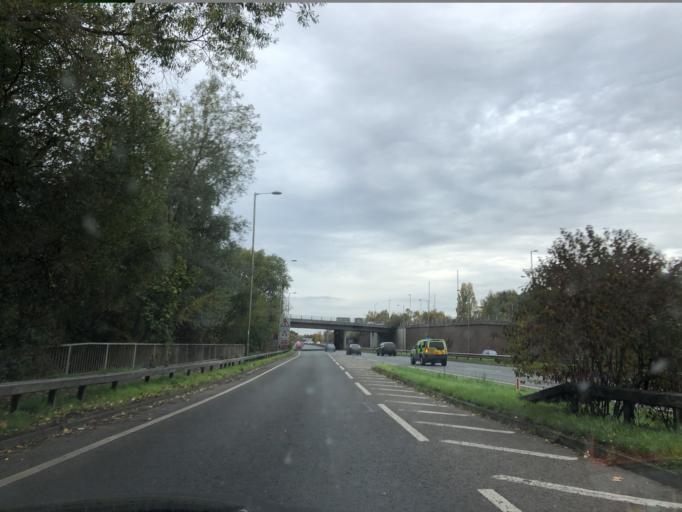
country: GB
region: England
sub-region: Surrey
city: Frimley
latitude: 51.3109
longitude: -0.7485
